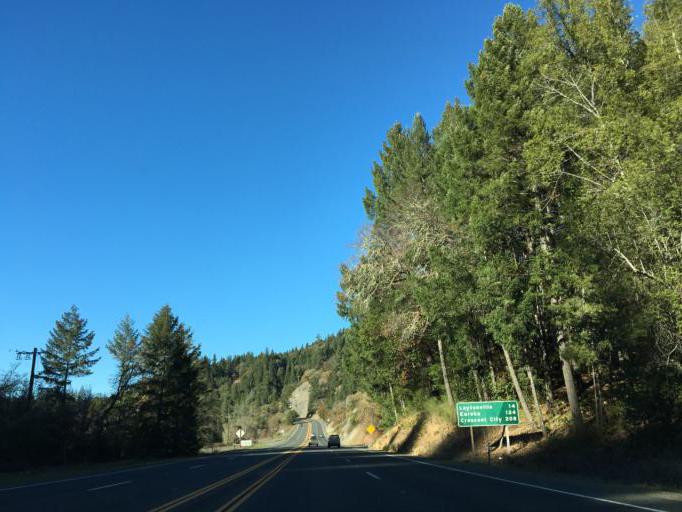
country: US
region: California
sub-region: Mendocino County
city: Brooktrails
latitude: 39.5175
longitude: -123.3912
